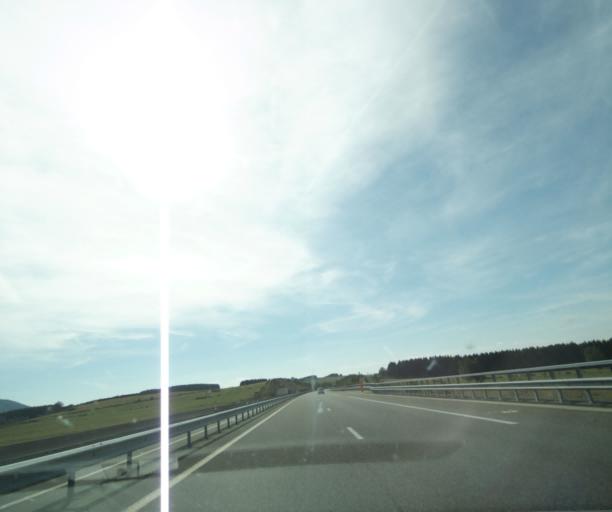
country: FR
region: Auvergne
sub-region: Departement du Puy-de-Dome
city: Saint-Ours
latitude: 45.8927
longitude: 2.9336
